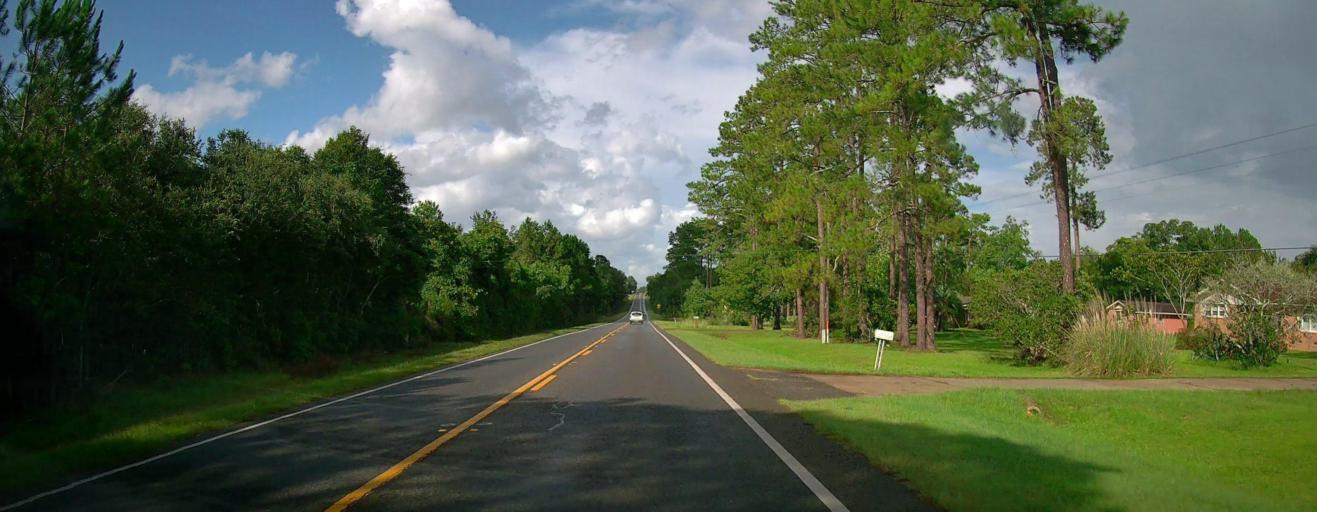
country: US
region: Georgia
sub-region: Coffee County
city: Douglas
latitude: 31.4766
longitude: -82.8716
